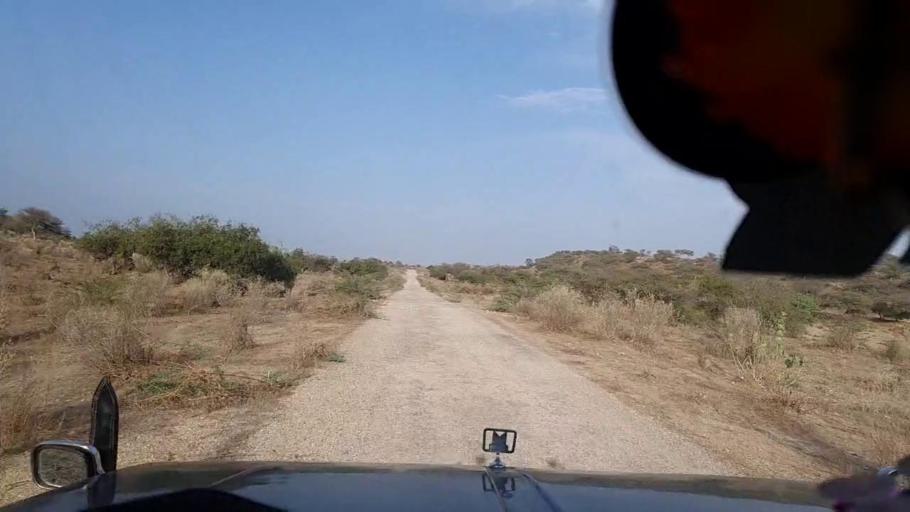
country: PK
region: Sindh
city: Diplo
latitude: 24.5565
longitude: 69.4708
